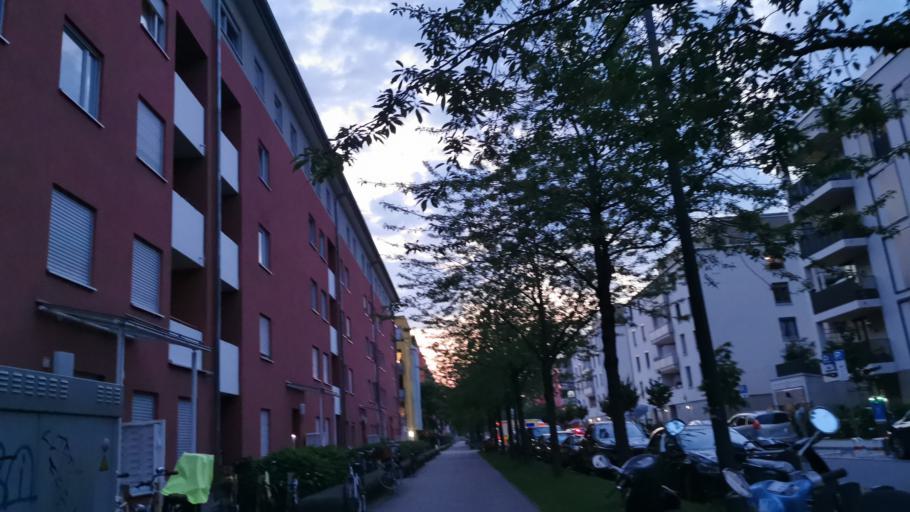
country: DE
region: Bavaria
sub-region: Upper Bavaria
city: Bogenhausen
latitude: 48.1807
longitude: 11.5935
